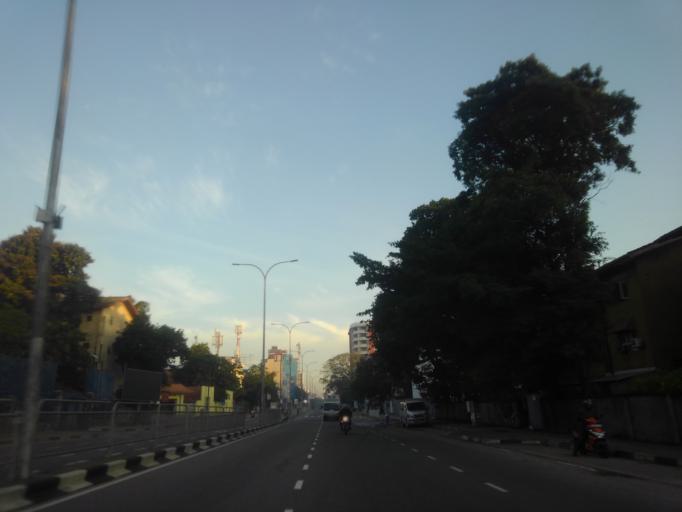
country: LK
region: Western
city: Pita Kotte
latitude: 6.9014
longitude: 79.8773
